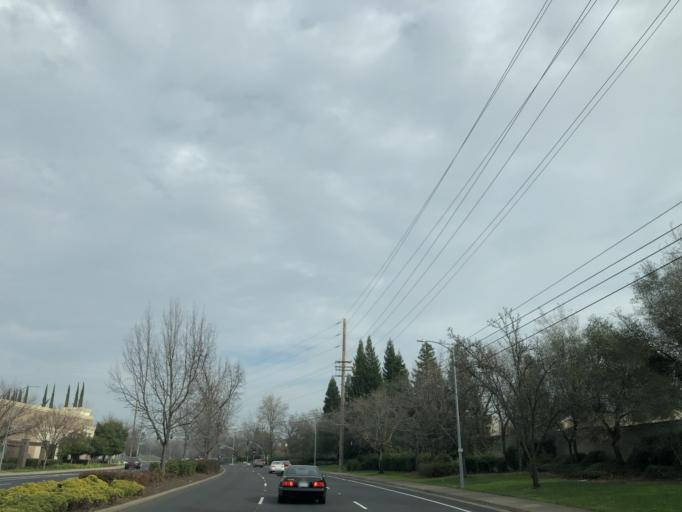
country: US
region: California
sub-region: Sacramento County
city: Folsom
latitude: 38.6548
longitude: -121.1753
